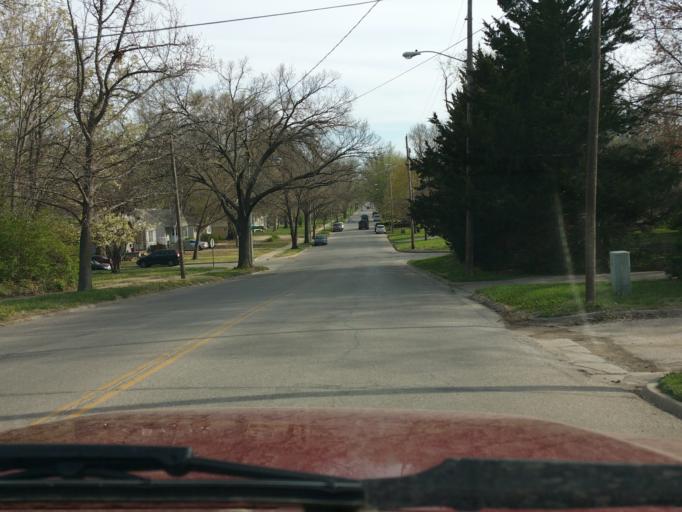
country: US
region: Kansas
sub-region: Riley County
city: Manhattan
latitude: 39.1917
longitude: -96.5666
